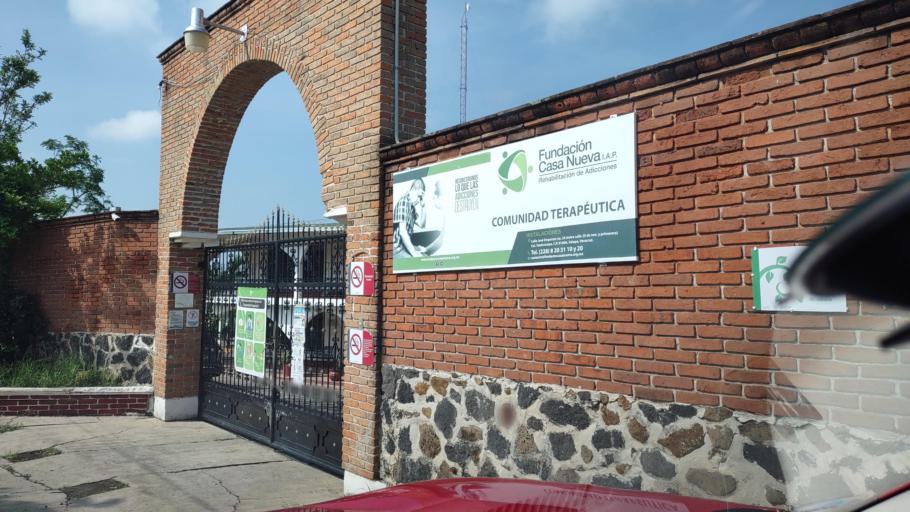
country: MX
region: Veracruz
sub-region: Coatepec
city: Bella Esperanza
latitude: 19.4534
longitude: -96.8317
